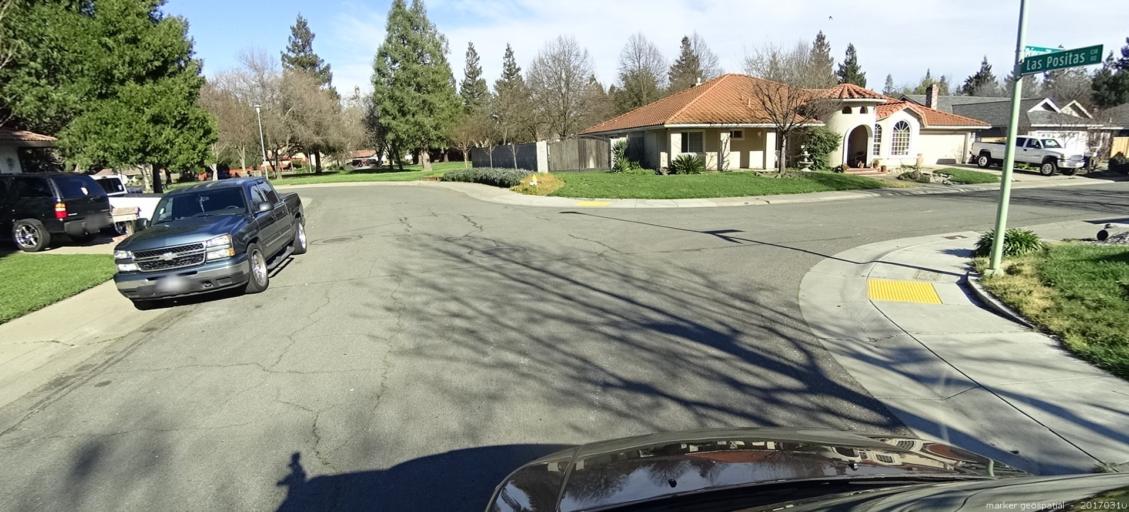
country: US
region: California
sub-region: Sacramento County
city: Parkway
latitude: 38.4935
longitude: -121.5305
